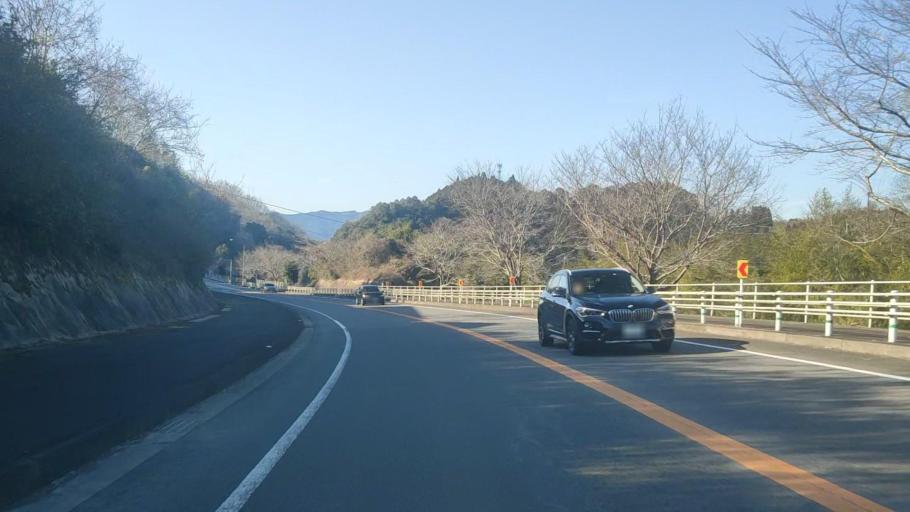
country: JP
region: Oita
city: Usuki
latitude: 33.0605
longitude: 131.6720
